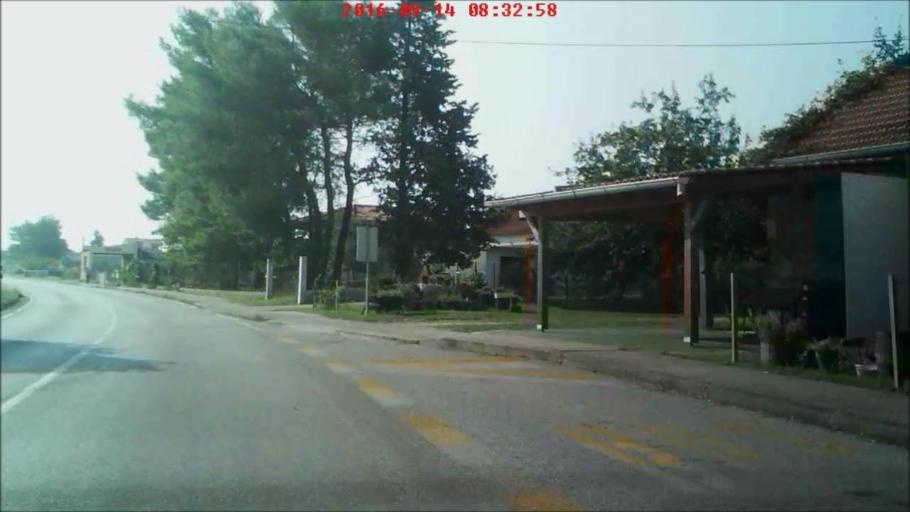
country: HR
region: Zadarska
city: Policnik
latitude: 44.1596
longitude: 15.3092
